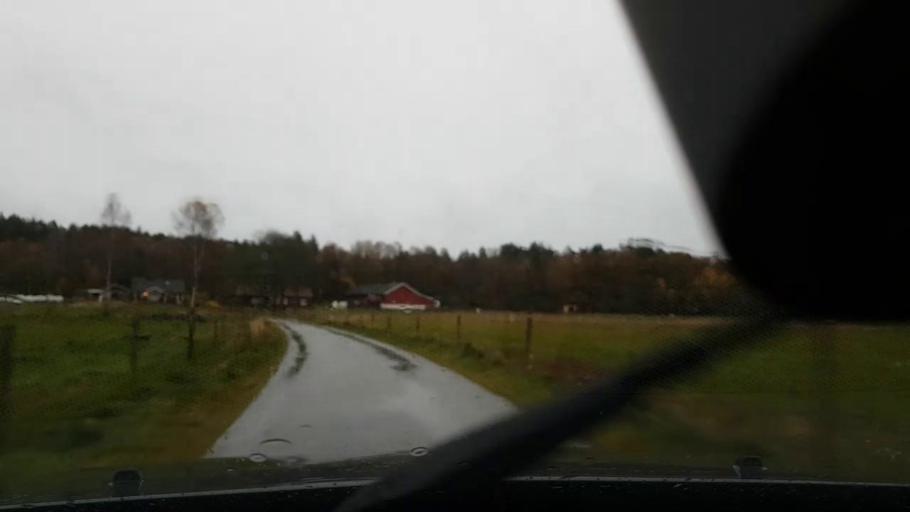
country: SE
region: Vaestra Goetaland
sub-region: Molndal
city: Lindome
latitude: 57.5790
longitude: 12.1100
